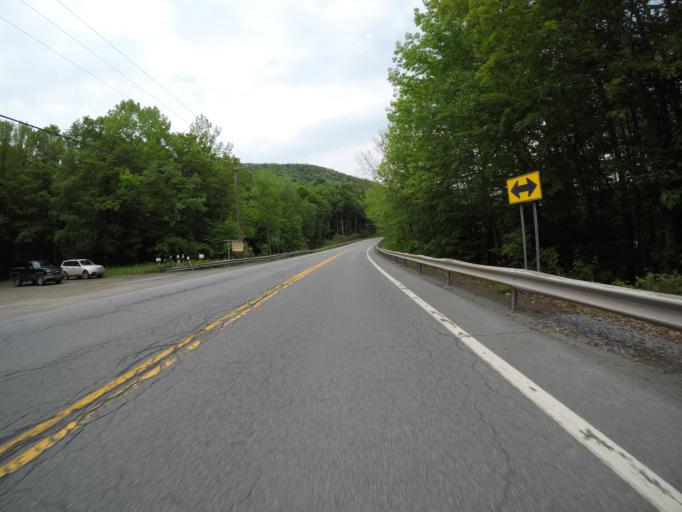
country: US
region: New York
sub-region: Sullivan County
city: Livingston Manor
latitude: 42.0722
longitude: -74.9088
